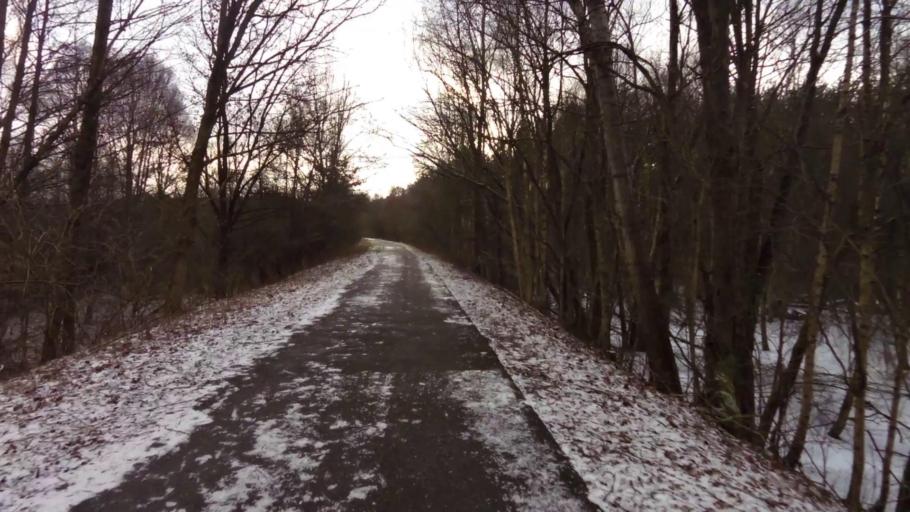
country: PL
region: West Pomeranian Voivodeship
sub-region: Powiat drawski
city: Zlocieniec
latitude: 53.5804
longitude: 16.0404
